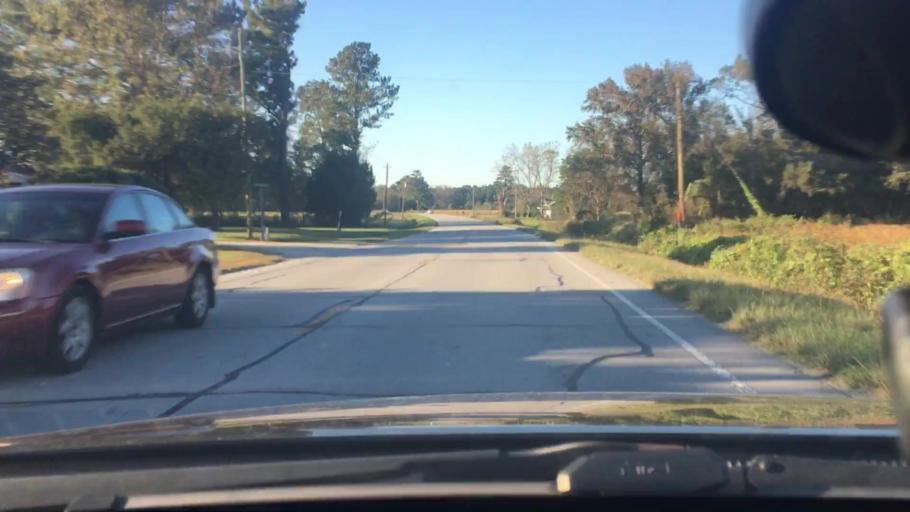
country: US
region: North Carolina
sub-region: Craven County
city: Vanceboro
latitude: 35.3176
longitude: -77.1633
